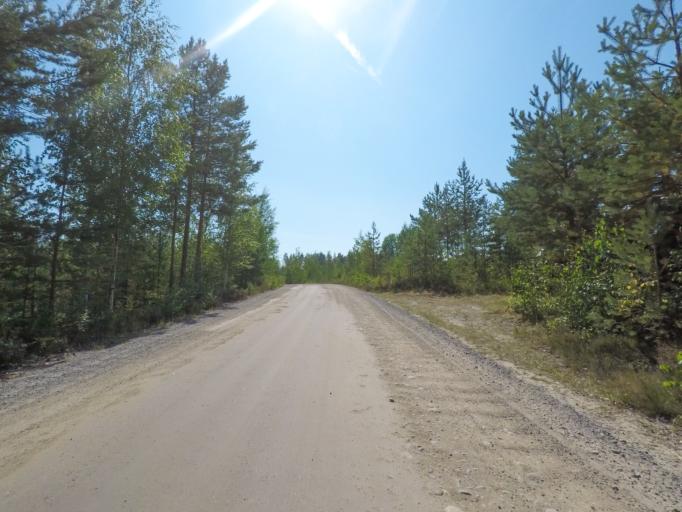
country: FI
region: Southern Savonia
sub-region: Mikkeli
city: Puumala
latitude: 61.4113
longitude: 28.0483
